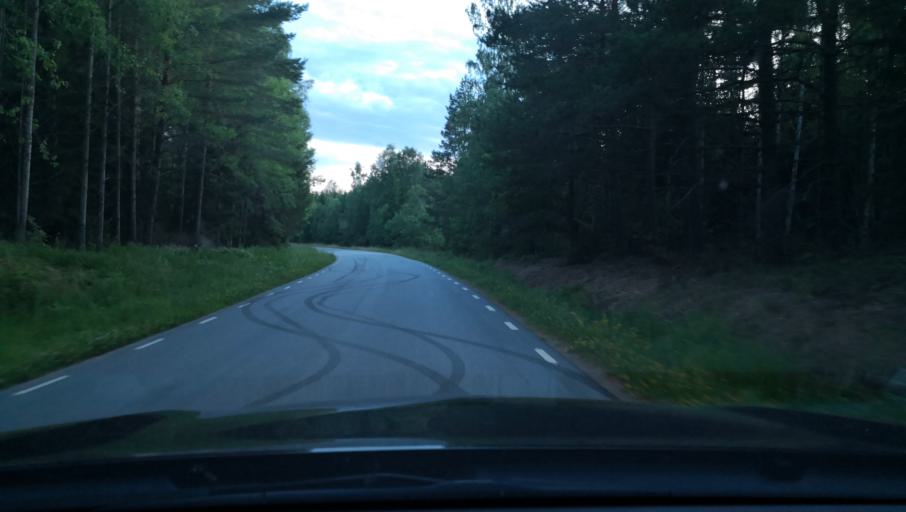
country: SE
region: Uppsala
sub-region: Osthammars Kommun
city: Bjorklinge
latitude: 60.0556
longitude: 17.5426
